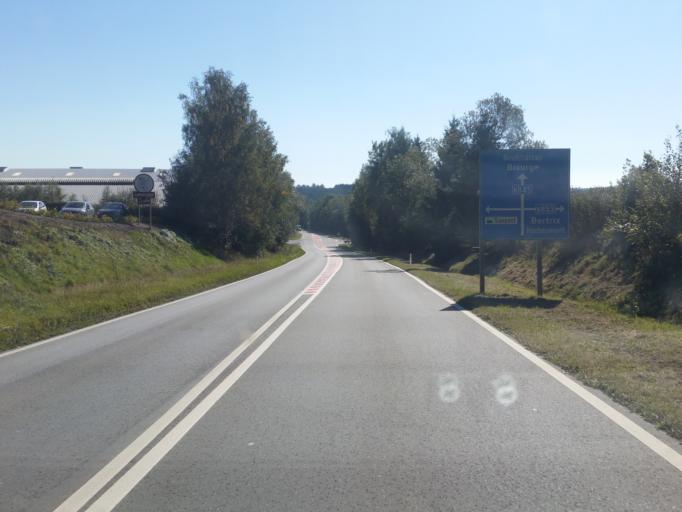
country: BE
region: Wallonia
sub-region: Province du Luxembourg
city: Bertrix
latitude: 49.8631
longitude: 5.2751
